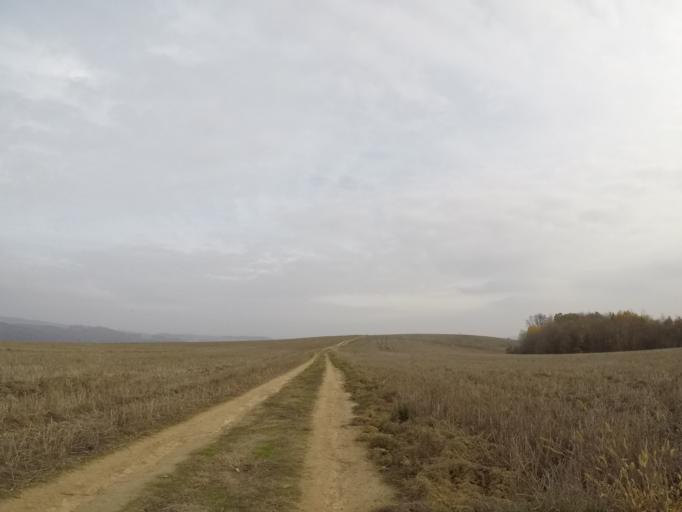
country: SK
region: Presovsky
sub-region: Okres Presov
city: Presov
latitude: 48.9400
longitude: 21.1546
